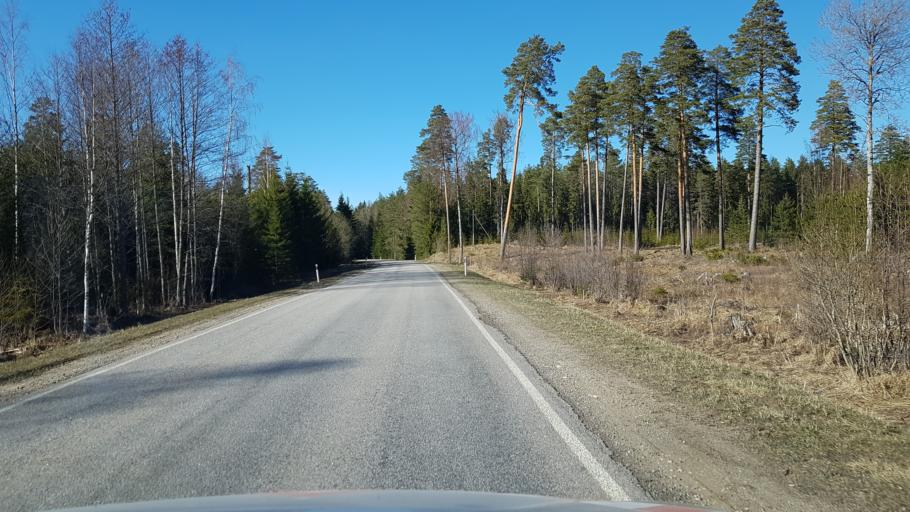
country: EE
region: Laeaene-Virumaa
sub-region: Vinni vald
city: Vinni
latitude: 59.2534
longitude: 26.6876
